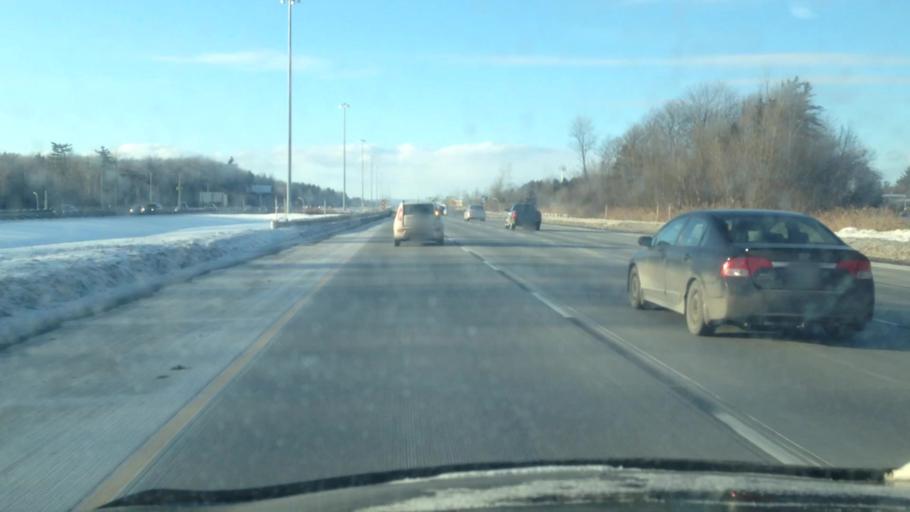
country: CA
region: Quebec
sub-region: Laurentides
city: Blainville
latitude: 45.6571
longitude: -73.8836
